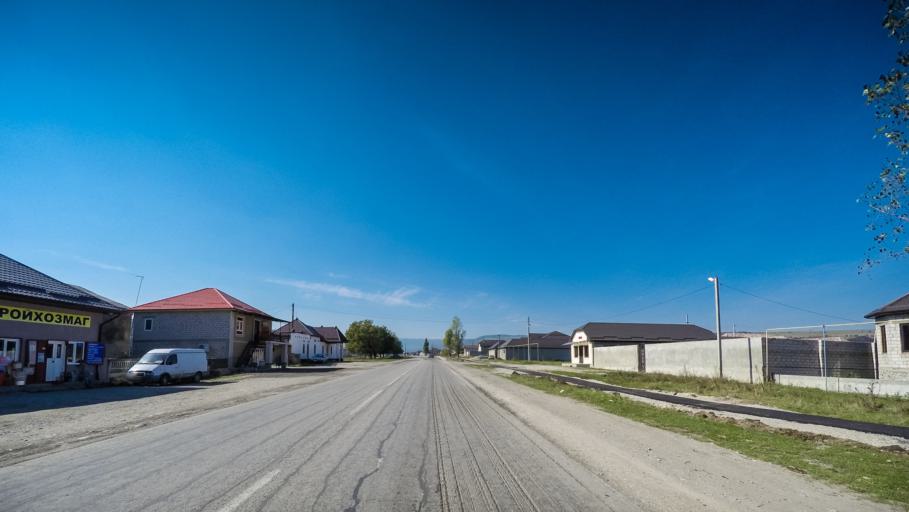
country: RU
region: Kabardino-Balkariya
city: Lechinkay
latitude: 43.5662
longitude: 43.4718
